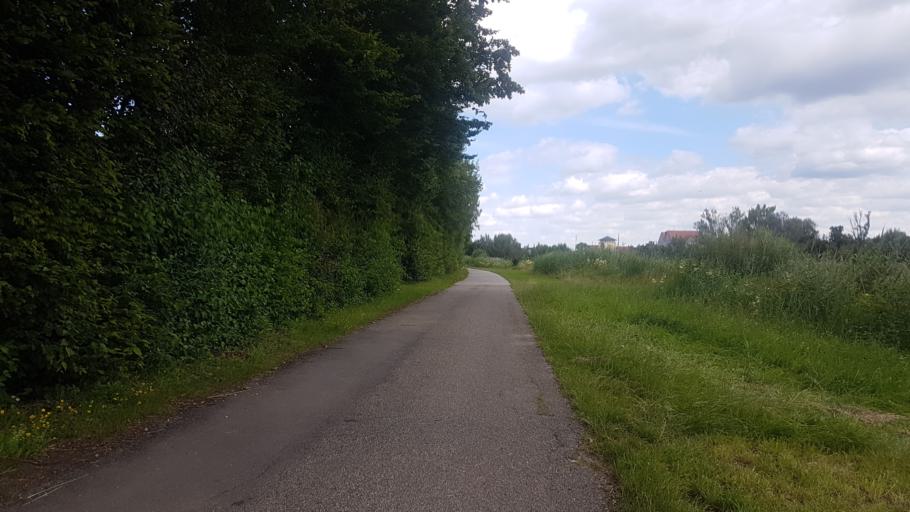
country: DE
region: Bavaria
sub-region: Regierungsbezirk Mittelfranken
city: Gunzenhausen
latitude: 49.1113
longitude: 10.7504
